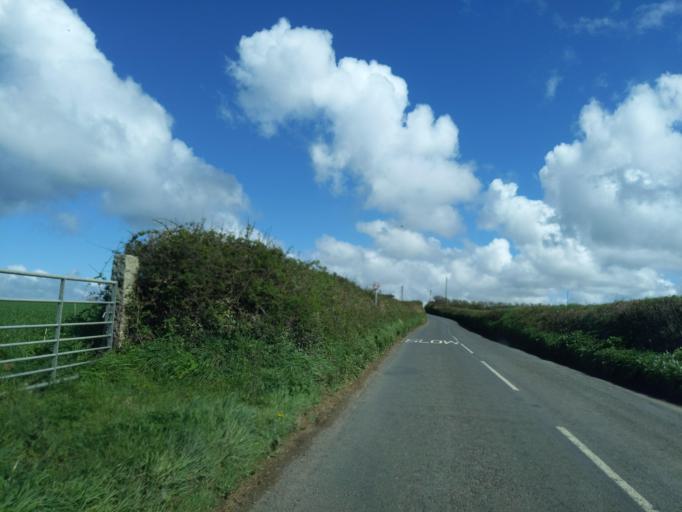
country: GB
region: England
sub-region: Cornwall
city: Wadebridge
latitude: 50.5735
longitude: -4.8369
